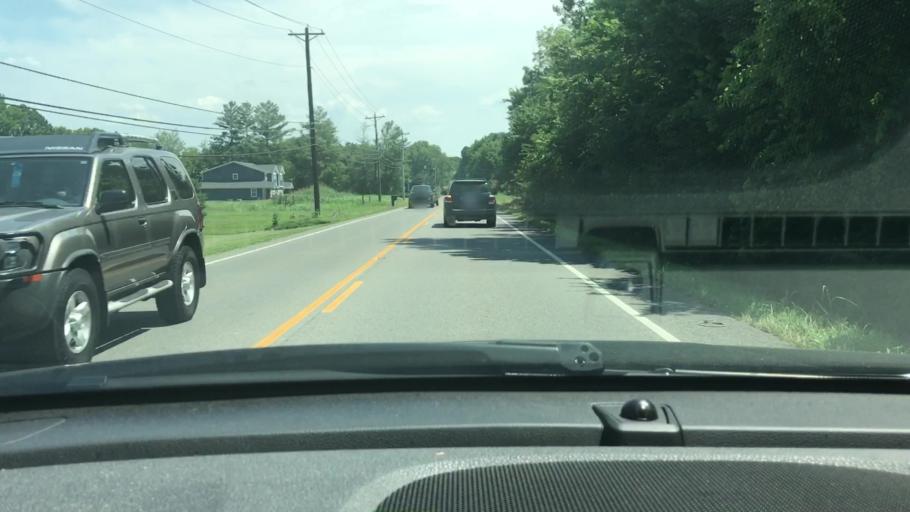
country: US
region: Tennessee
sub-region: Sumner County
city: Shackle Island
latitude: 36.3623
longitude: -86.6111
